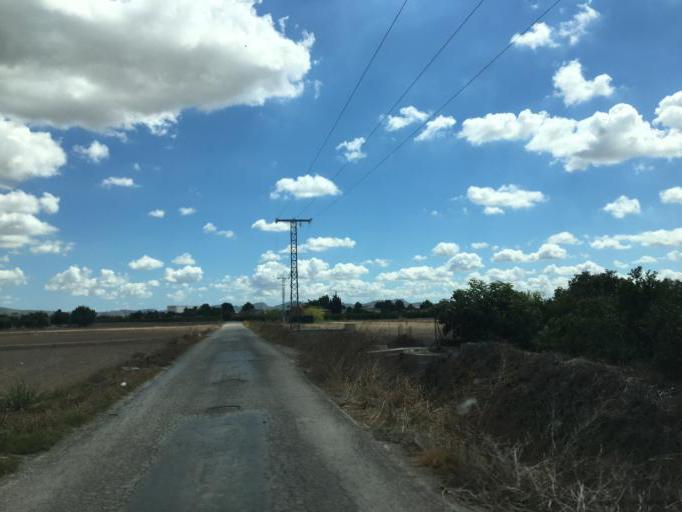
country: ES
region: Murcia
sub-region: Murcia
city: Santomera
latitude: 38.0477
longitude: -1.0443
